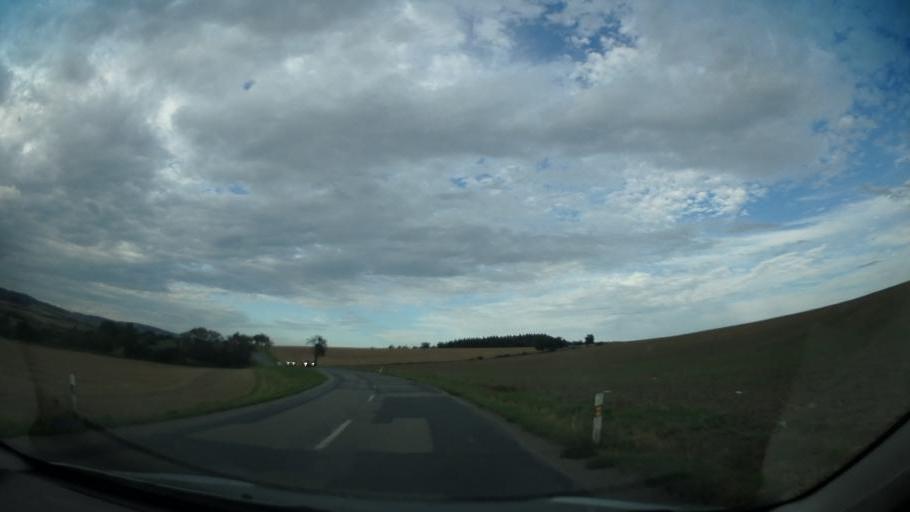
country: CZ
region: South Moravian
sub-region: Okres Blansko
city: Boskovice
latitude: 49.5006
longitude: 16.6680
